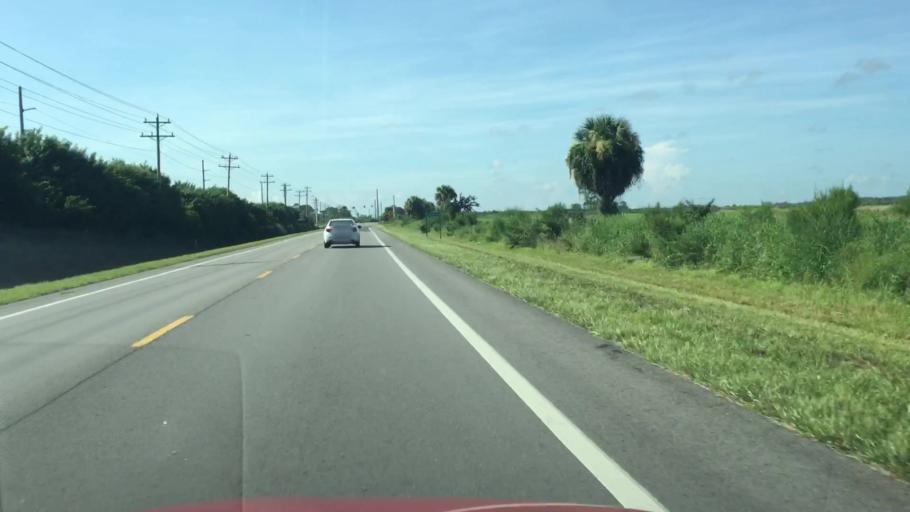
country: US
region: Florida
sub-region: Collier County
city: Immokalee
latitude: 26.3781
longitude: -81.4171
